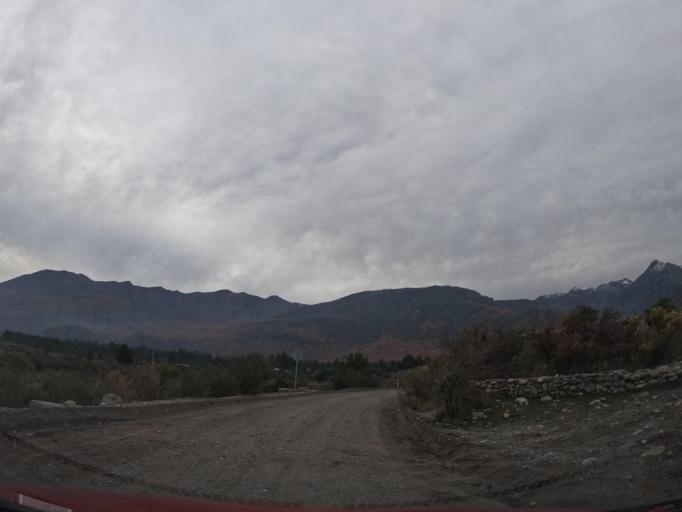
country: CL
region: Maule
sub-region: Provincia de Linares
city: Colbun
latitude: -35.7065
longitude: -71.0775
